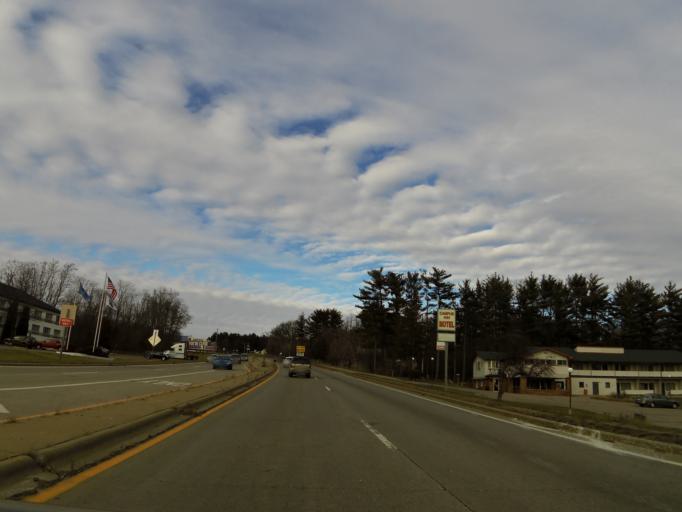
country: US
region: Wisconsin
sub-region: Sauk County
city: West Baraboo
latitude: 43.4772
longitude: -89.7688
